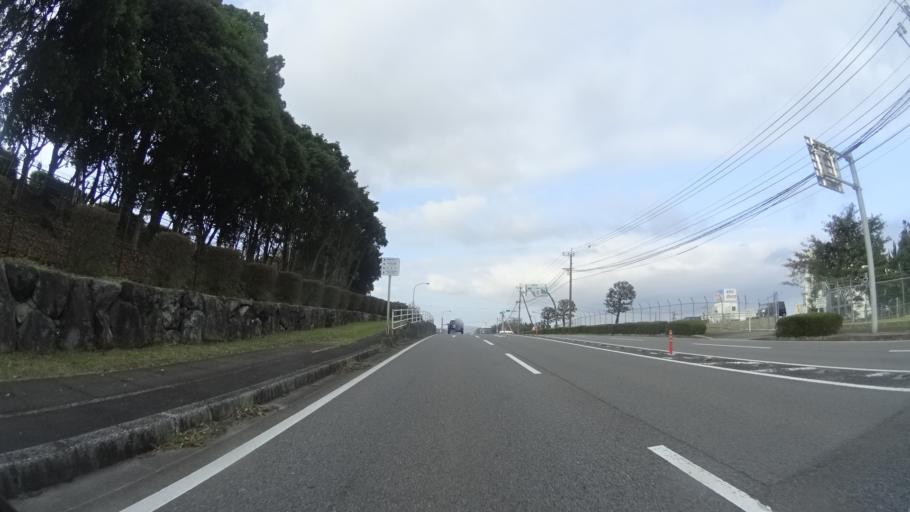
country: JP
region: Oita
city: Beppu
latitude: 33.2949
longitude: 131.4605
